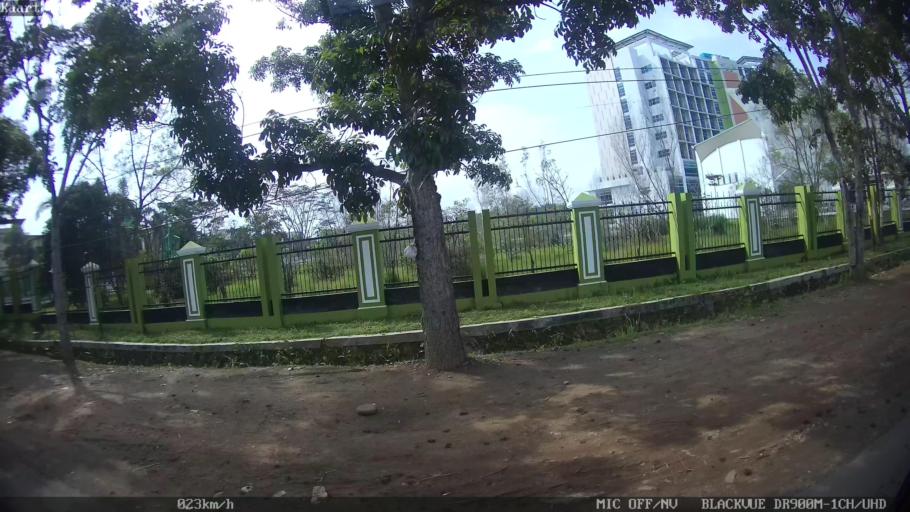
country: ID
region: Lampung
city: Kedaton
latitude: -5.3786
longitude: 105.3034
